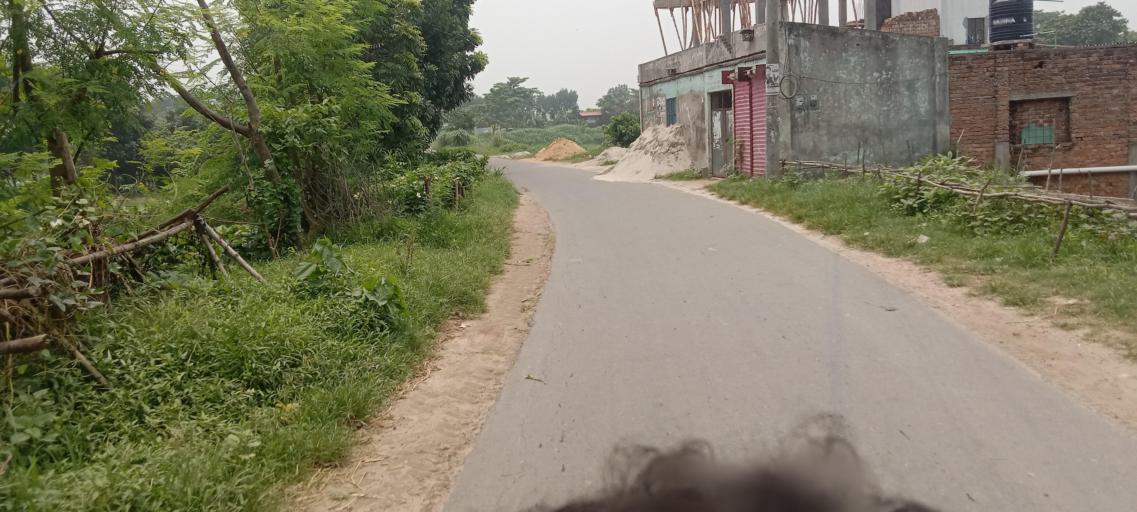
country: BD
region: Dhaka
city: Azimpur
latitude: 23.7465
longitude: 90.3019
